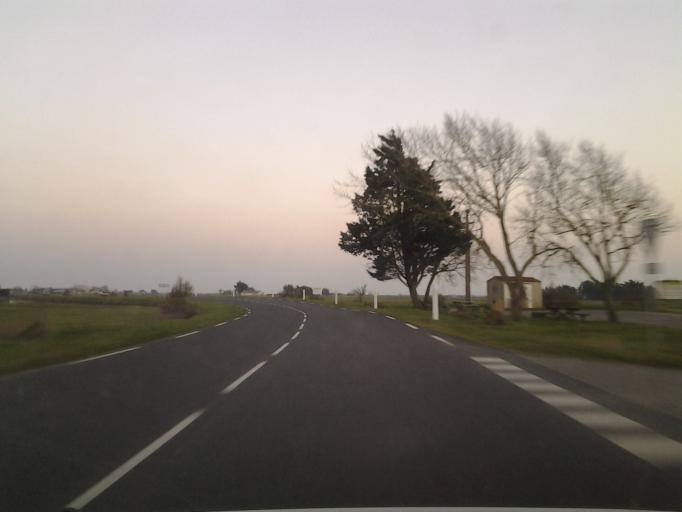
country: FR
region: Pays de la Loire
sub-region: Departement de la Vendee
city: Beauvoir-sur-Mer
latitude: 46.9187
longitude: -2.0816
